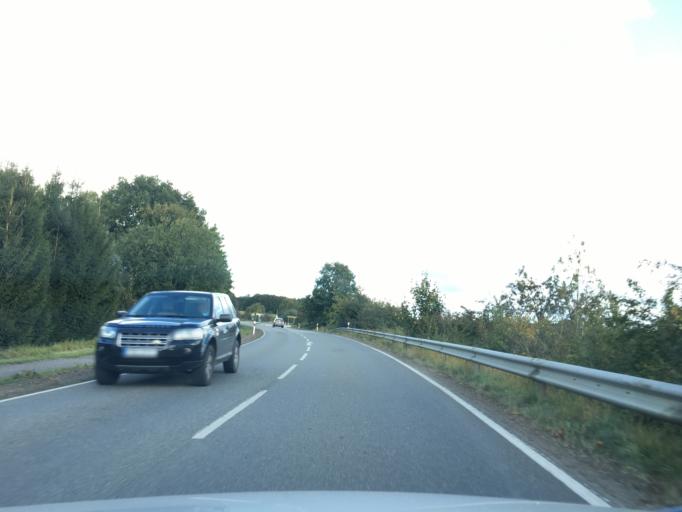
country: DE
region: Schleswig-Holstein
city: Rodenbek
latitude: 54.3023
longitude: 10.0163
